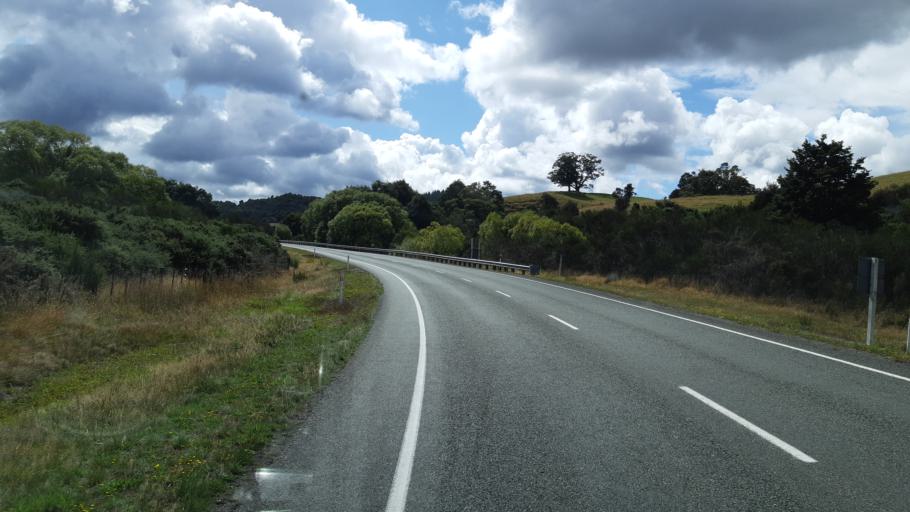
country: NZ
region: Tasman
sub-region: Tasman District
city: Wakefield
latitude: -41.6452
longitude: 172.6580
